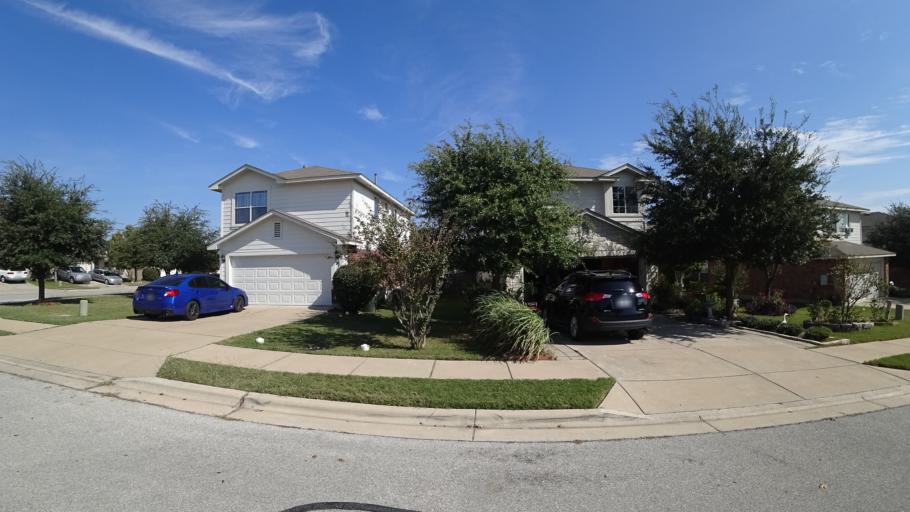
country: US
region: Texas
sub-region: Travis County
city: Pflugerville
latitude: 30.4258
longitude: -97.6372
